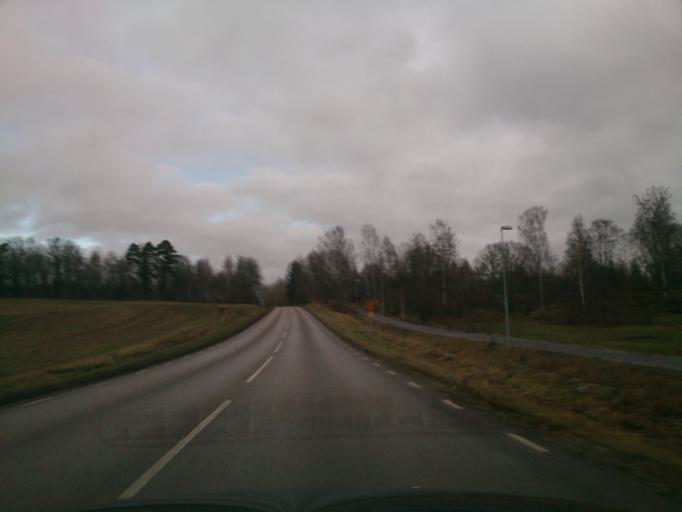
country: SE
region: OEstergoetland
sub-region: Atvidabergs Kommun
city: Atvidaberg
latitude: 58.2194
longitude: 15.9739
